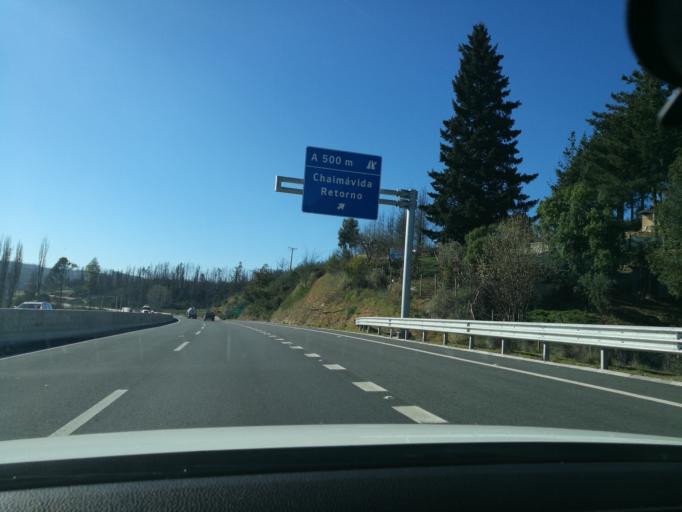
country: CL
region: Biobio
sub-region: Provincia de Concepcion
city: Chiguayante
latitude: -36.8568
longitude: -72.8869
